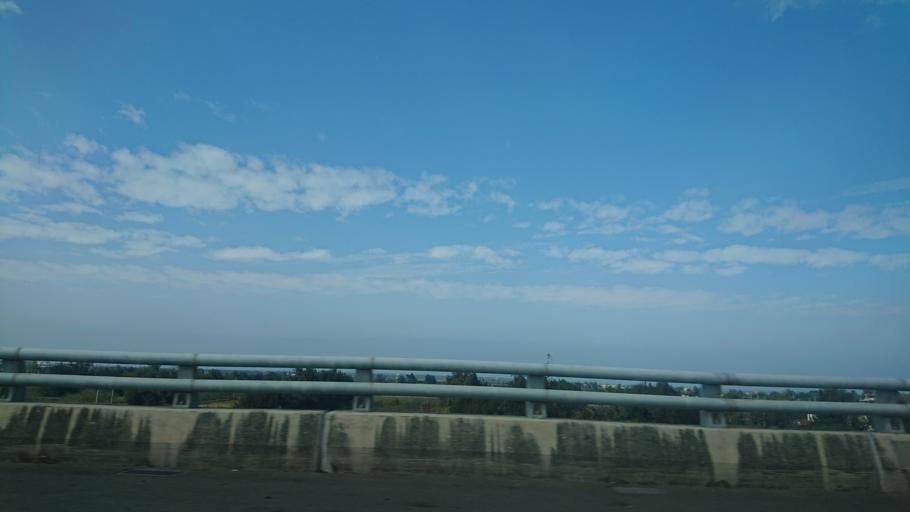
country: TW
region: Taiwan
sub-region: Yunlin
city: Douliu
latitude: 23.8519
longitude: 120.2954
